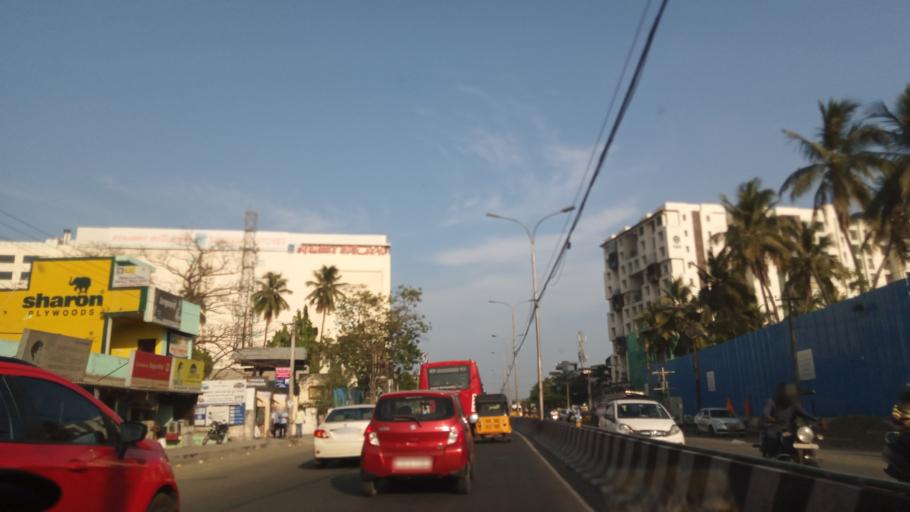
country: IN
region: Tamil Nadu
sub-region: Thiruvallur
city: Porur
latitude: 13.0328
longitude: 80.1626
